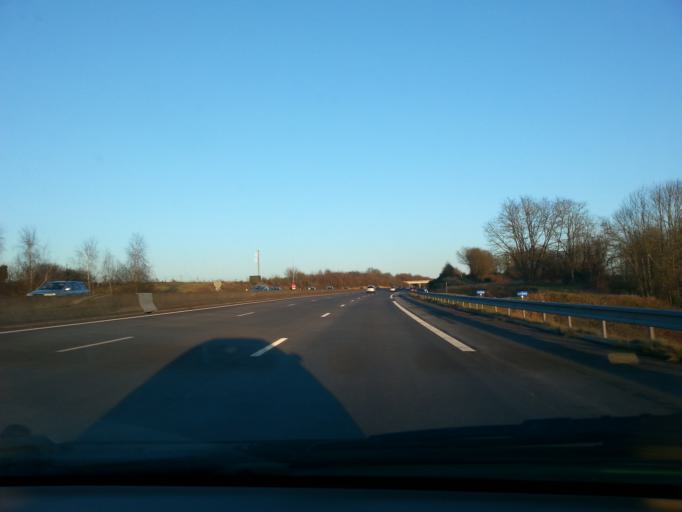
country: FR
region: Lower Normandy
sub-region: Departement de l'Orne
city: Ceton
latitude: 48.1745
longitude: 0.7551
